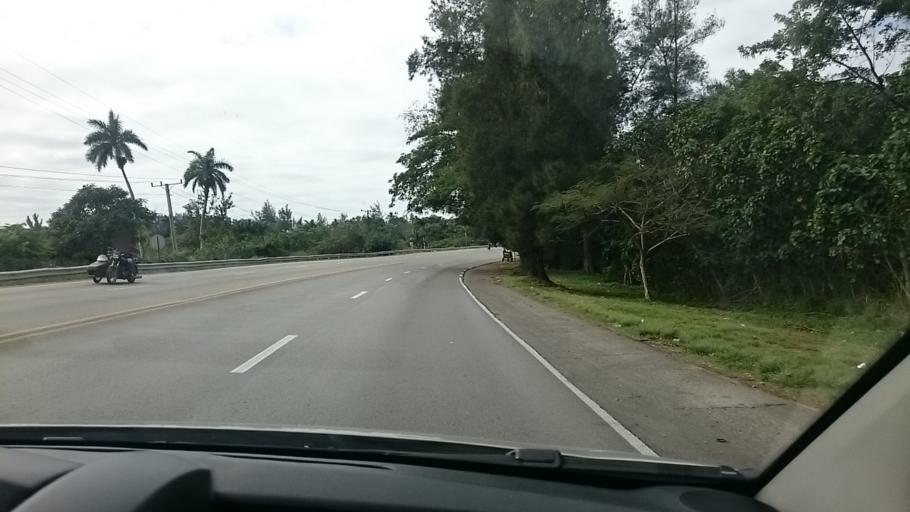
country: CU
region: La Habana
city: Alamar
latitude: 23.1461
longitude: -82.2820
